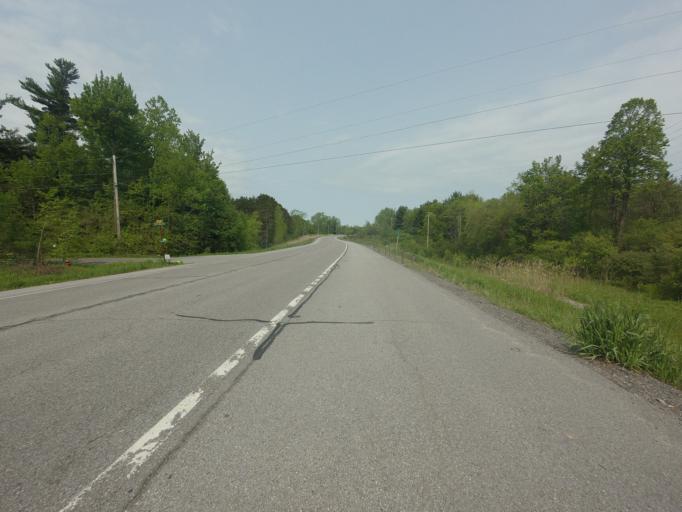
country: US
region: New York
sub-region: Jefferson County
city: Dexter
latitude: 44.0091
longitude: -76.0144
